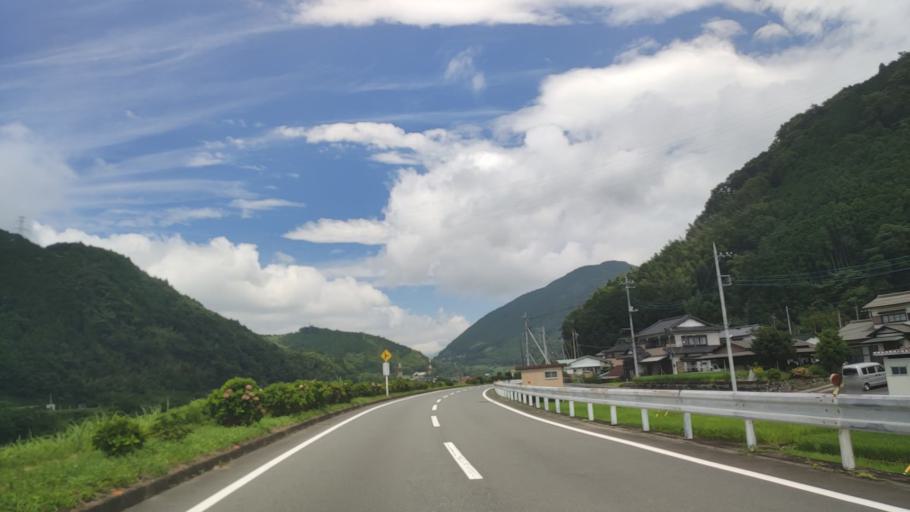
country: JP
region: Shizuoka
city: Fujinomiya
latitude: 35.2303
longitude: 138.5129
